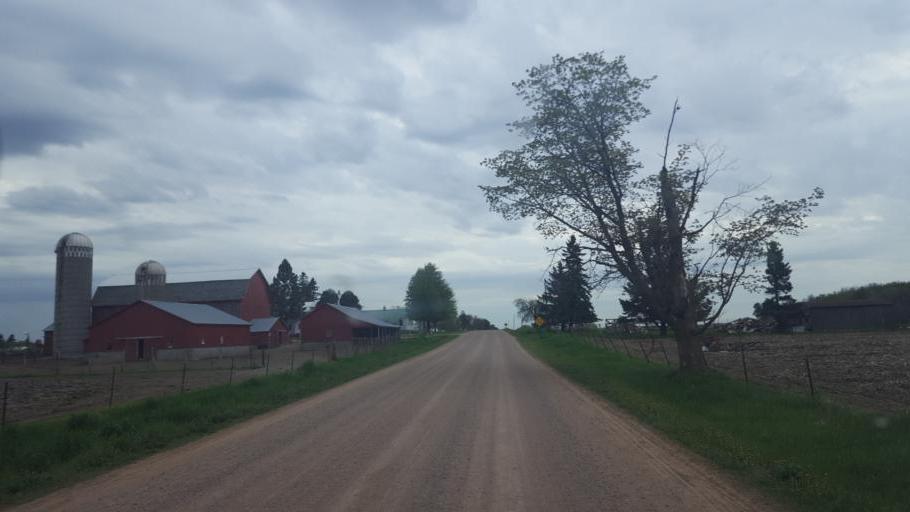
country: US
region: Wisconsin
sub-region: Marathon County
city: Spencer
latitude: 44.6344
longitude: -90.3766
